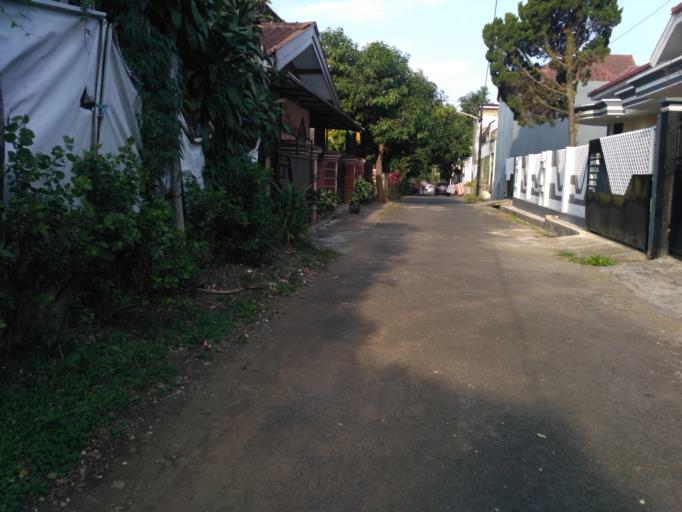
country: ID
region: East Java
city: Malang
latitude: -7.9390
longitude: 112.6260
